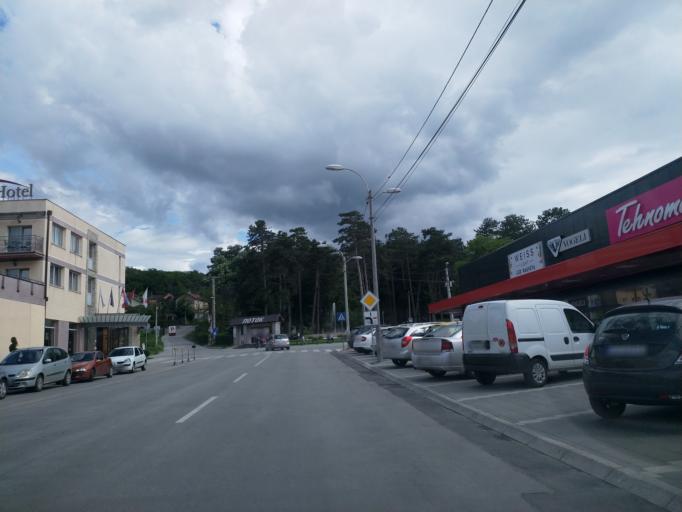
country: RS
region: Central Serbia
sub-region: Pomoravski Okrug
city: Jagodina
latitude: 43.9662
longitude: 21.2660
